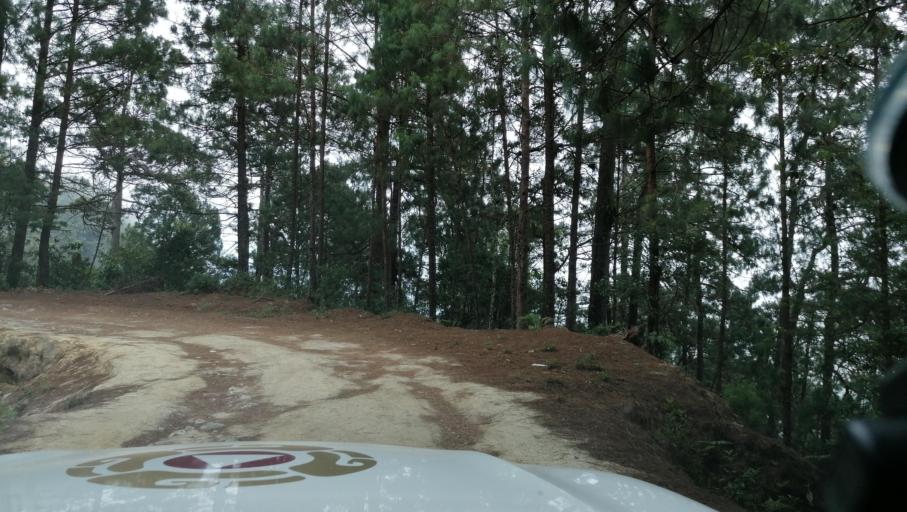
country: MX
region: Chiapas
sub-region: Tapachula
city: Canton Villaflor
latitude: 15.1982
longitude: -92.2321
